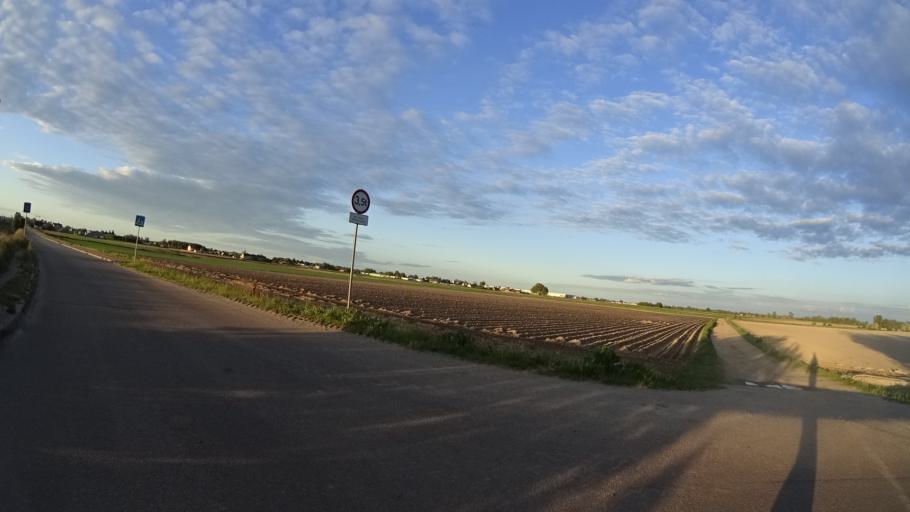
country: PL
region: Masovian Voivodeship
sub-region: Powiat warszawski zachodni
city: Jozefow
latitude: 52.2001
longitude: 20.7437
